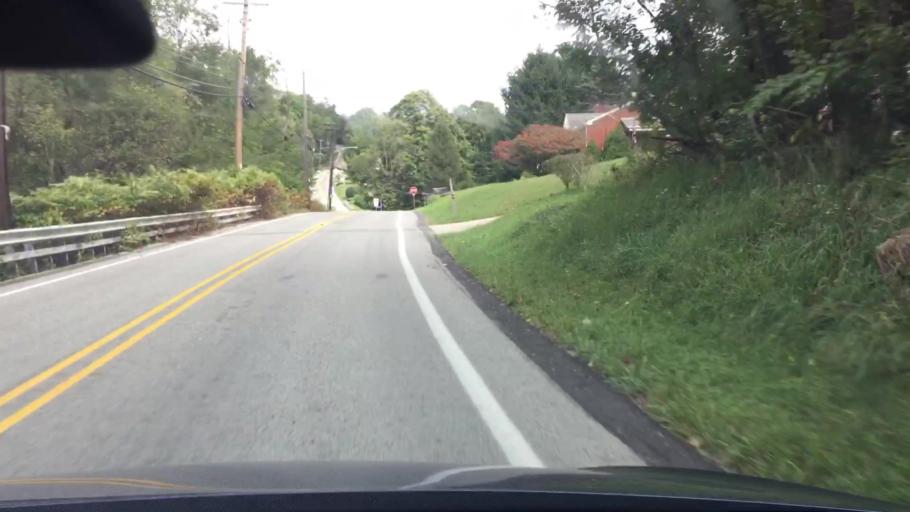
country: US
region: Pennsylvania
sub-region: Allegheny County
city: Penn Hills
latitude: 40.4941
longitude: -79.8094
